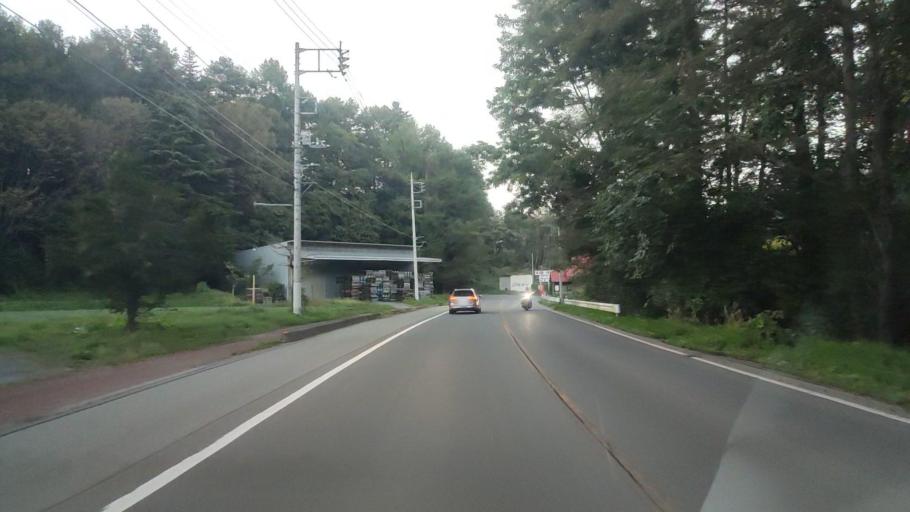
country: JP
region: Gunma
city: Nakanojomachi
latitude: 36.5139
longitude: 138.5976
